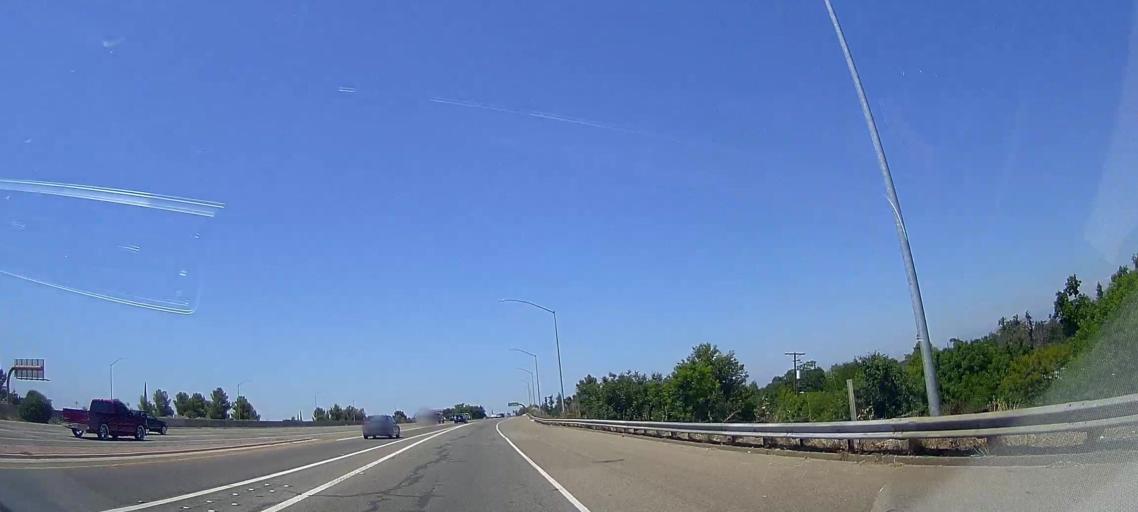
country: US
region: California
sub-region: Fresno County
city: Fresno
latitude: 36.7587
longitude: -119.7751
